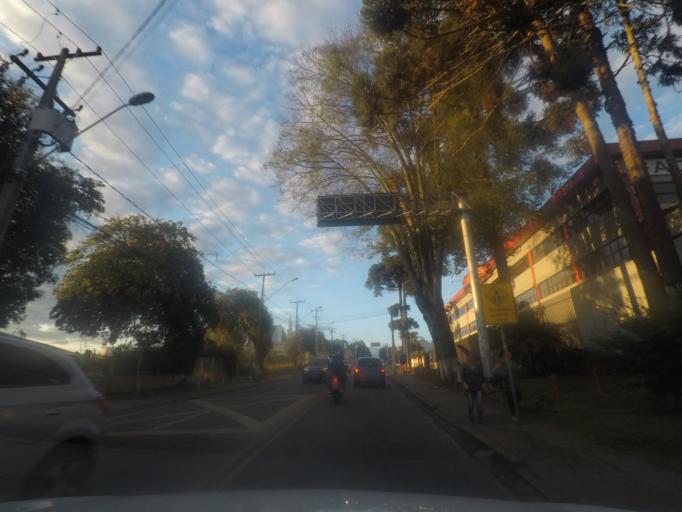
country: BR
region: Parana
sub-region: Pinhais
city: Pinhais
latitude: -25.4452
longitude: -49.1895
